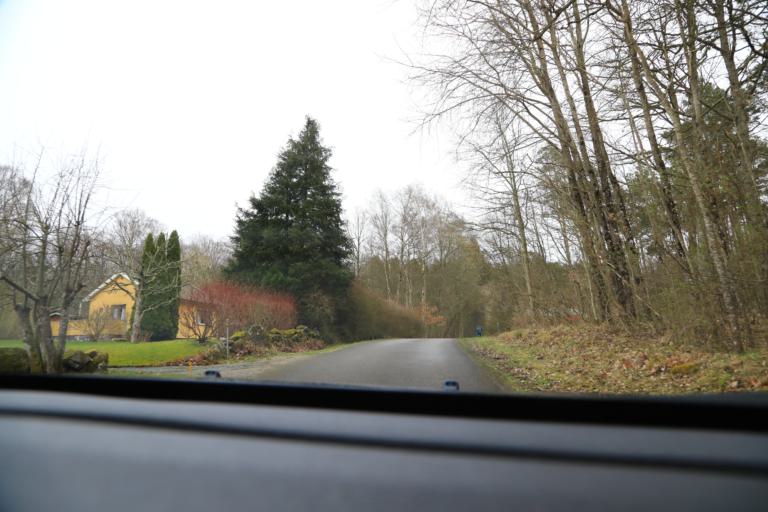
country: SE
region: Halland
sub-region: Kungsbacka Kommun
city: Frillesas
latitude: 57.3085
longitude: 12.1797
